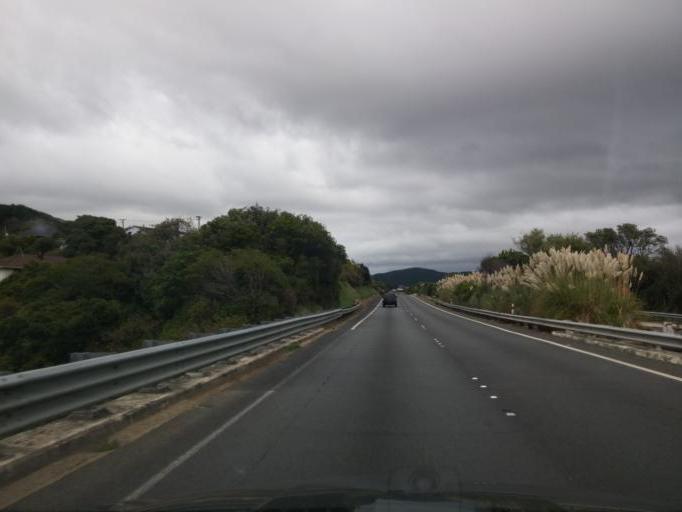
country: NZ
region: Wellington
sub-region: Porirua City
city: Porirua
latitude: -41.1589
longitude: 174.8372
